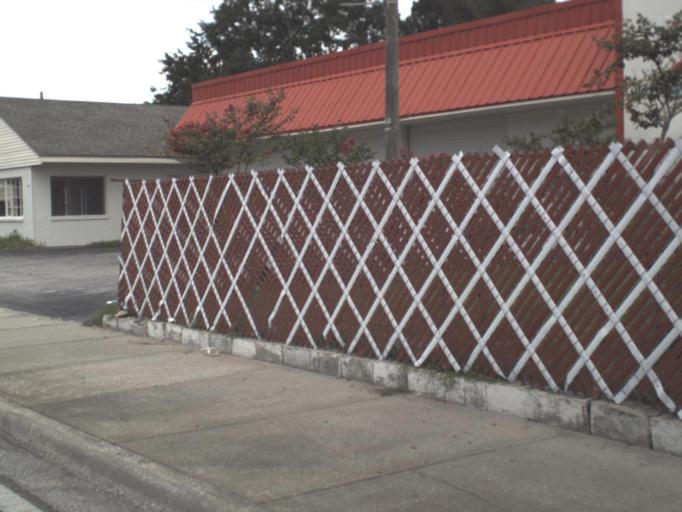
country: US
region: Florida
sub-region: Hillsborough County
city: Tampa
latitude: 27.9962
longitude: -82.4486
